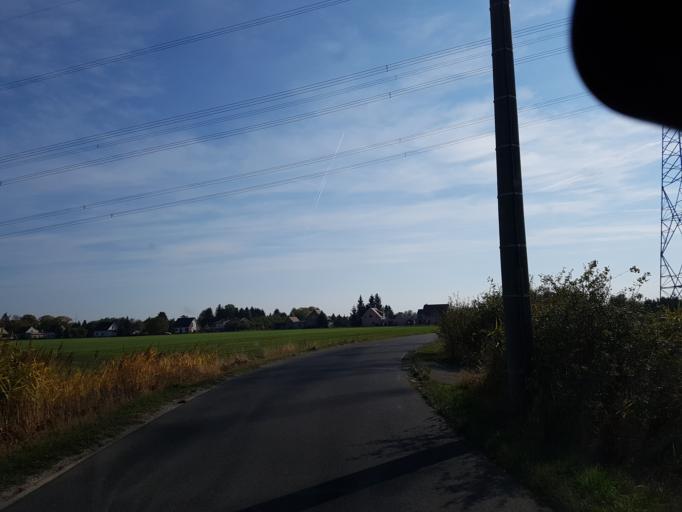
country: DE
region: Brandenburg
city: Doberlug-Kirchhain
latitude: 51.6433
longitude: 13.5476
